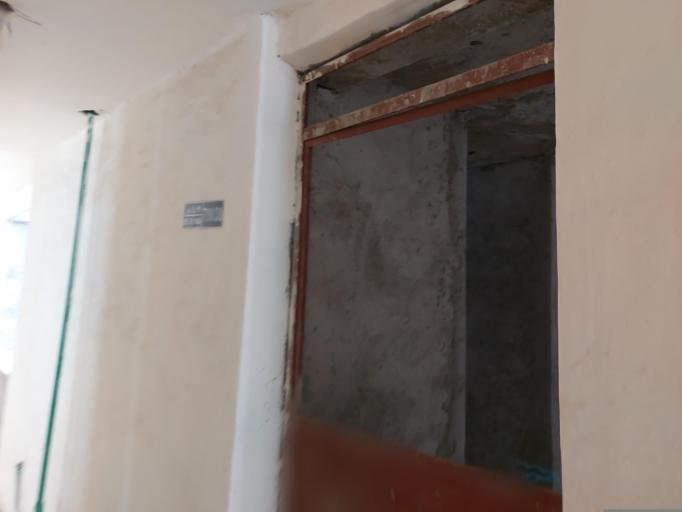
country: ET
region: Adis Abeba
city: Addis Ababa
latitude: 8.9617
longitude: 38.8753
